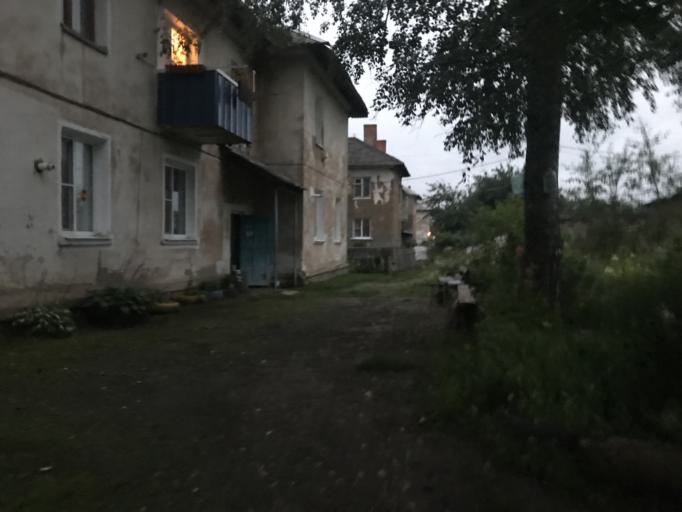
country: RU
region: Tula
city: Priupskiy
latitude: 53.9396
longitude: 37.7058
